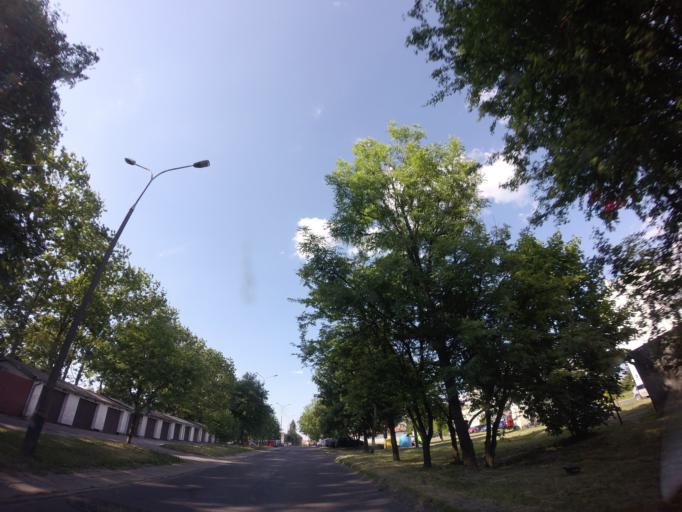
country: PL
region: West Pomeranian Voivodeship
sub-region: Powiat mysliborski
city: Barlinek
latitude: 52.9930
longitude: 15.2025
